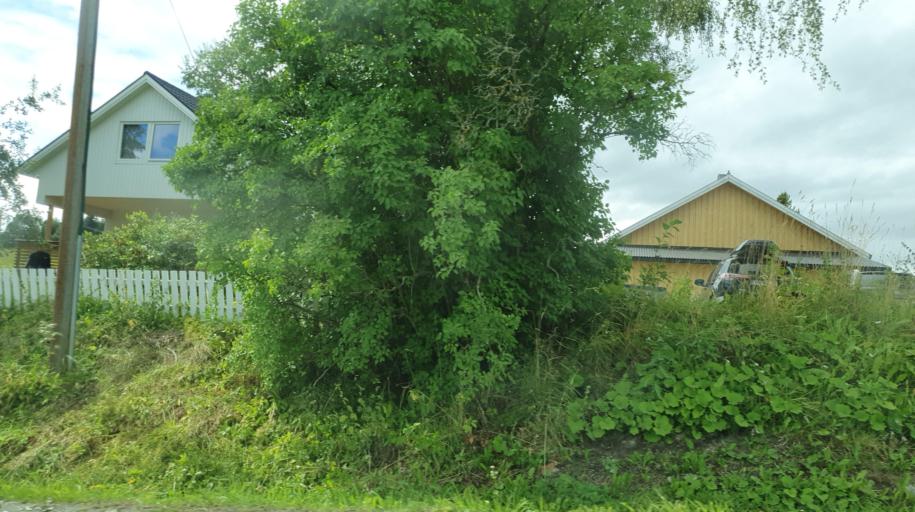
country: NO
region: Nord-Trondelag
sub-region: Stjordal
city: Stjordalshalsen
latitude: 63.5047
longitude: 11.0827
